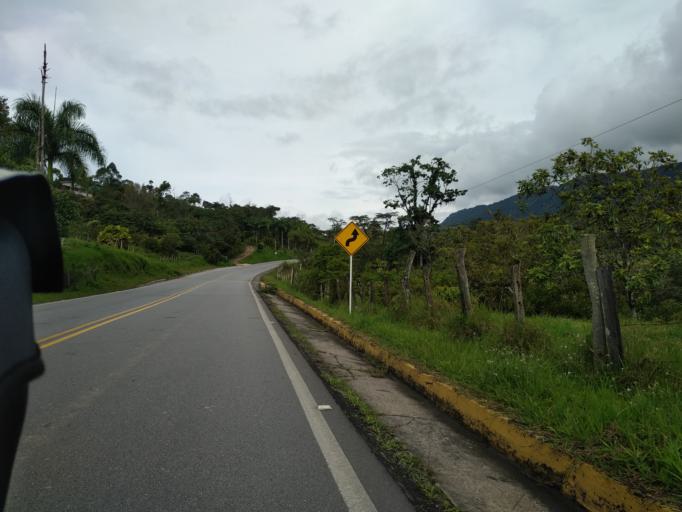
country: CO
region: Santander
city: Suaita
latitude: 6.0984
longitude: -73.3786
